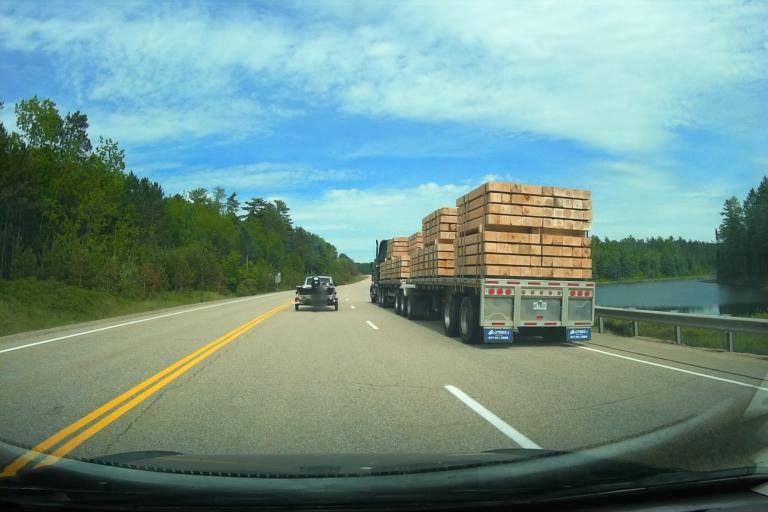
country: CA
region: Ontario
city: Mattawa
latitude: 46.2744
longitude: -78.9673
